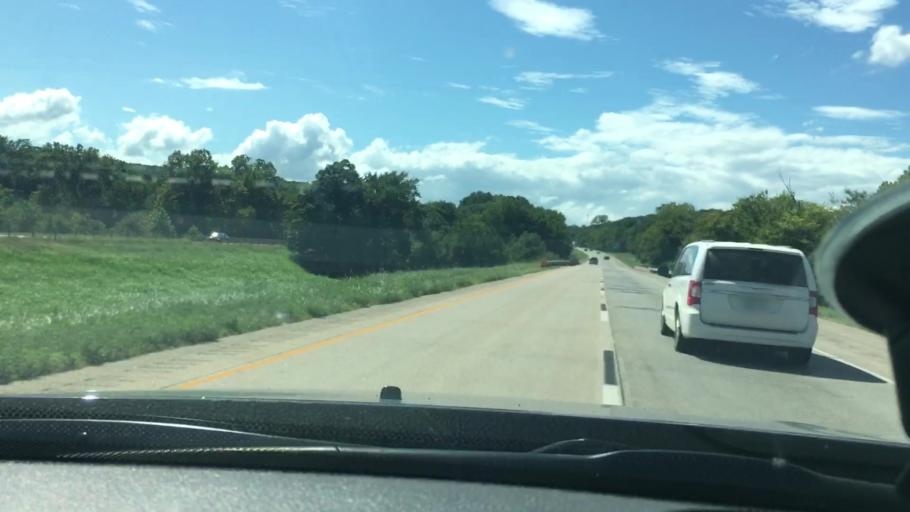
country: US
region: Oklahoma
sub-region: Sequoyah County
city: Vian
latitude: 35.4898
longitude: -94.9820
